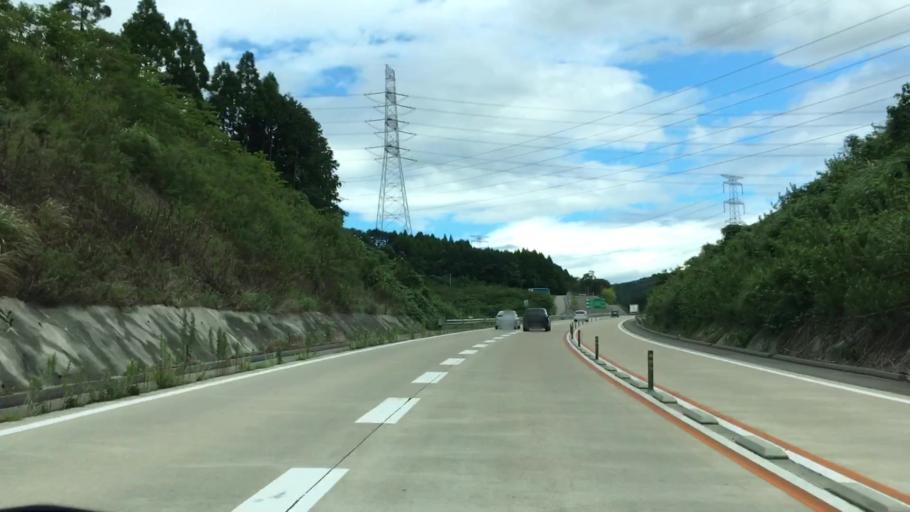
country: JP
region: Saga Prefecture
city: Imaricho-ko
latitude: 33.3521
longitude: 129.9247
